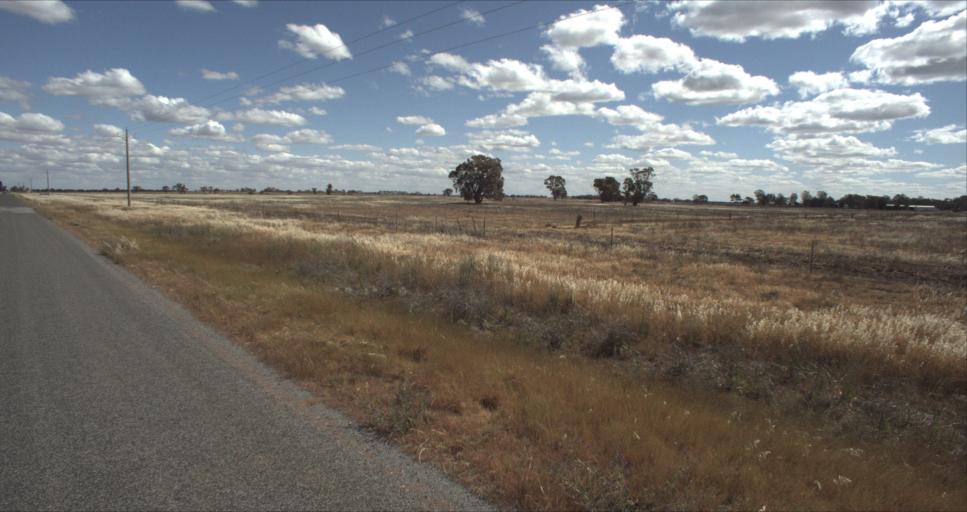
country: AU
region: New South Wales
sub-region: Leeton
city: Leeton
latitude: -34.4646
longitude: 146.2521
